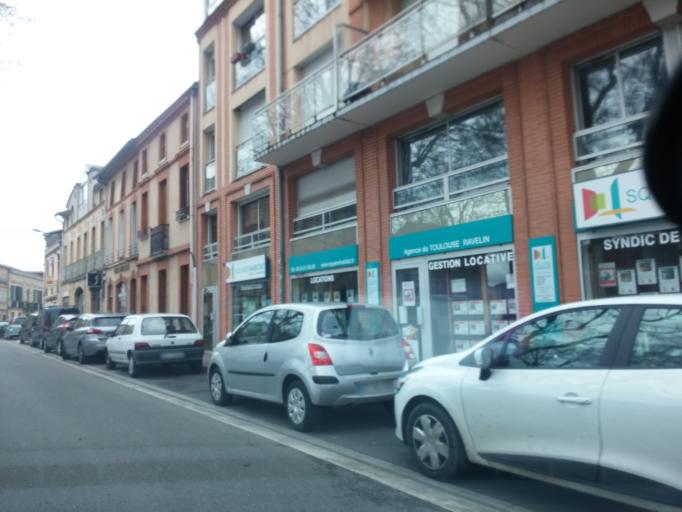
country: FR
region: Midi-Pyrenees
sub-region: Departement de la Haute-Garonne
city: Toulouse
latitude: 43.5992
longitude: 1.4289
